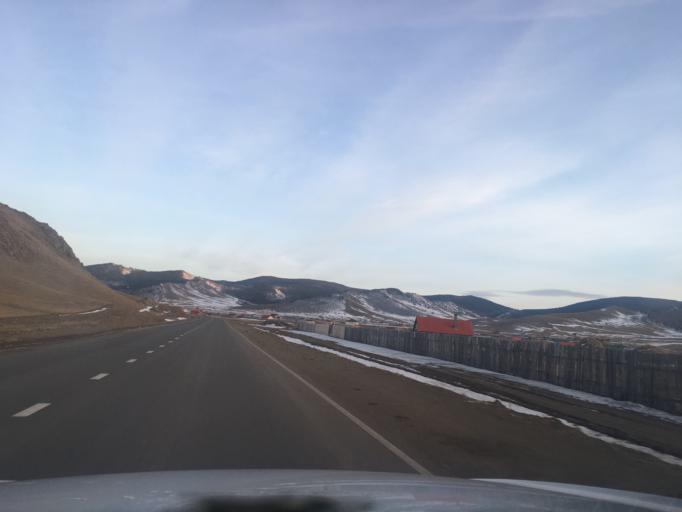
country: MN
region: Ulaanbaatar
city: Ulaanbaatar
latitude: 48.0989
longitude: 106.7378
